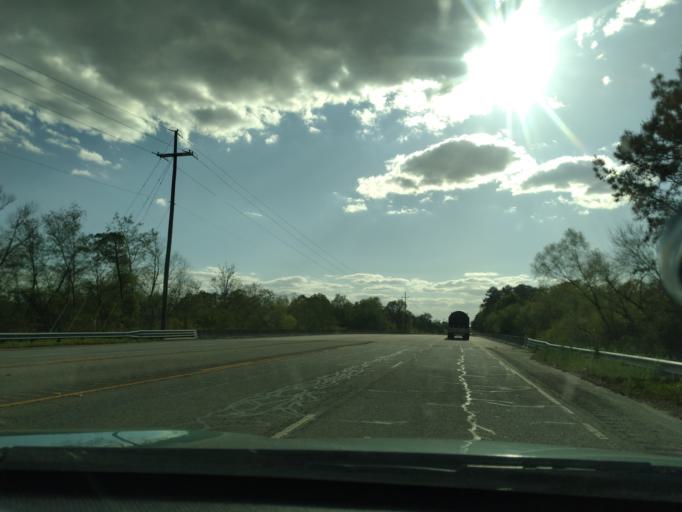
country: US
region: South Carolina
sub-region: Williamsburg County
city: Kingstree
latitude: 33.6615
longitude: -79.8399
